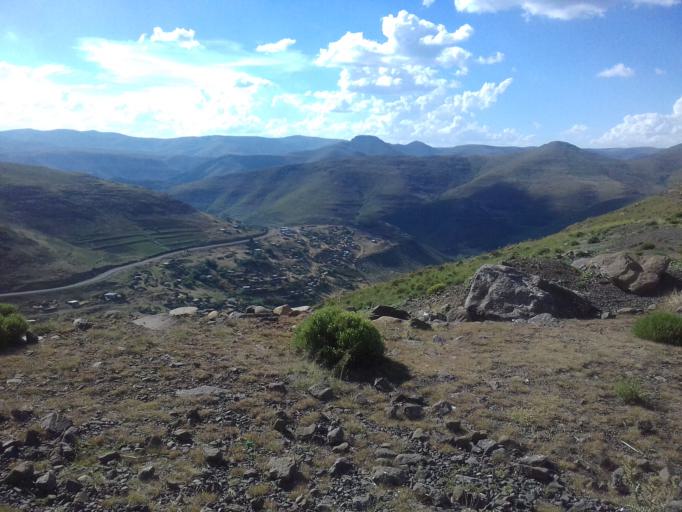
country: LS
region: Thaba-Tseka
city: Thaba-Tseka
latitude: -29.5198
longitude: 28.3355
